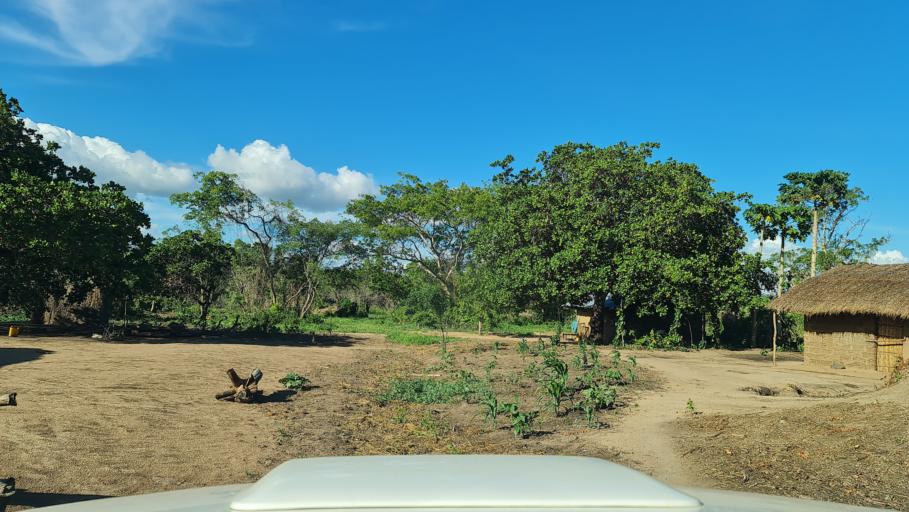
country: MZ
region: Nampula
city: Ilha de Mocambique
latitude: -15.2439
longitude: 40.1802
